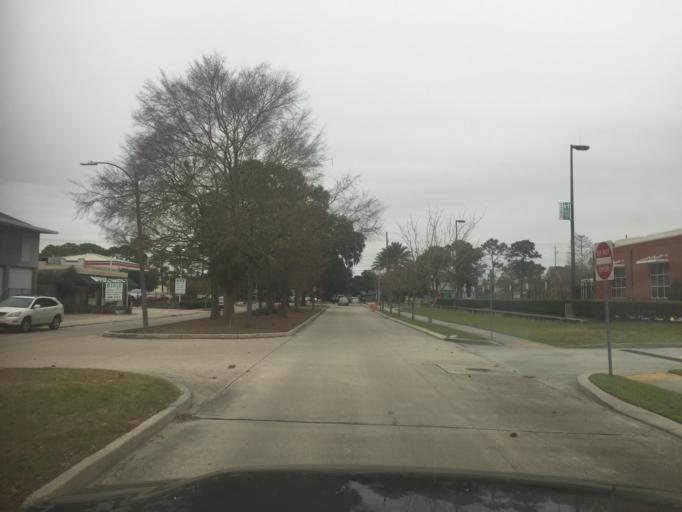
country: US
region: Louisiana
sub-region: Jefferson Parish
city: Metairie
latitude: 30.0032
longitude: -90.1028
